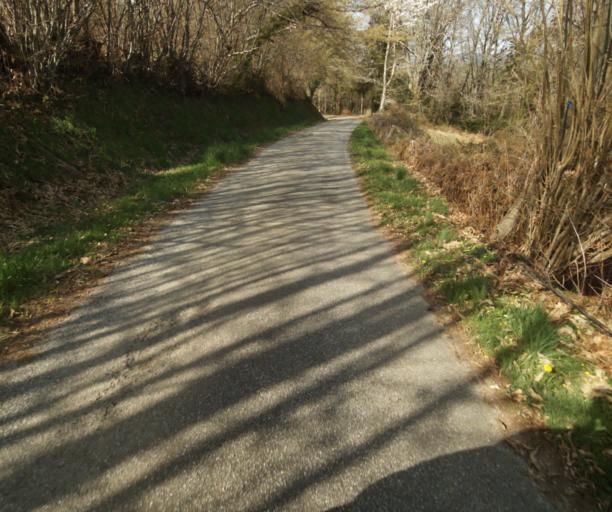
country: FR
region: Limousin
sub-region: Departement de la Correze
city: Naves
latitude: 45.3499
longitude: 1.7625
